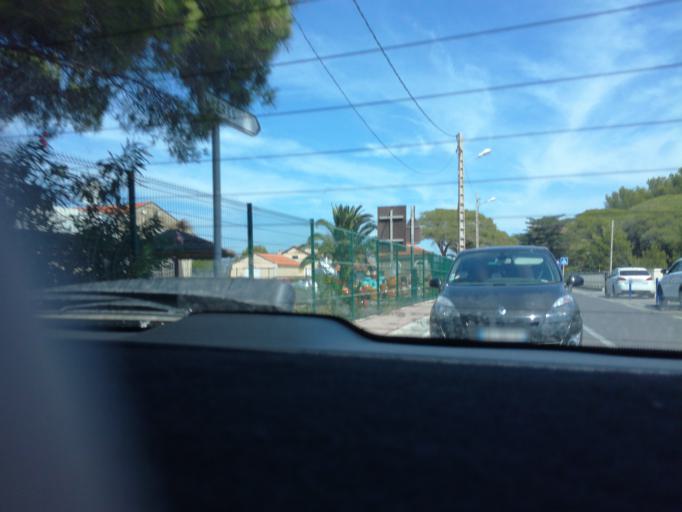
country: FR
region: Provence-Alpes-Cote d'Azur
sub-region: Departement du Var
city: Hyeres
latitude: 43.0660
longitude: 6.1471
